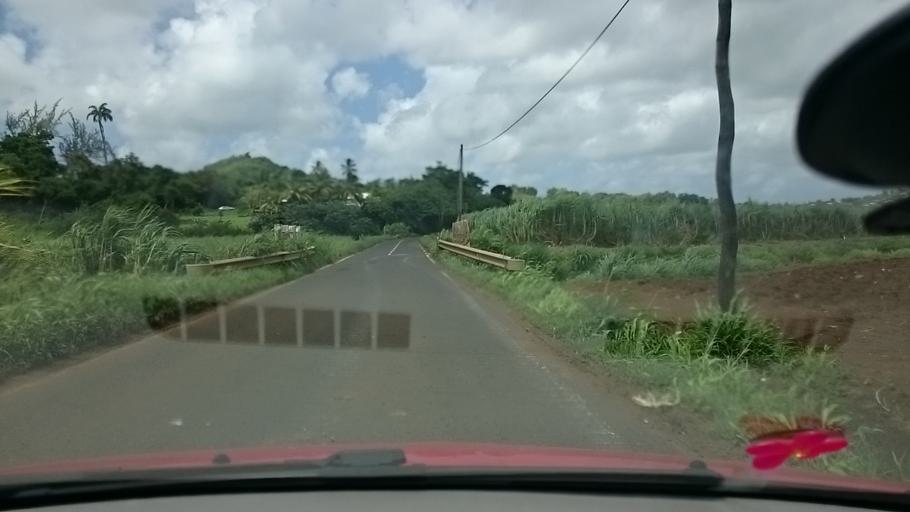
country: MQ
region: Martinique
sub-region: Martinique
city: Saint-Esprit
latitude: 14.5788
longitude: -60.9284
